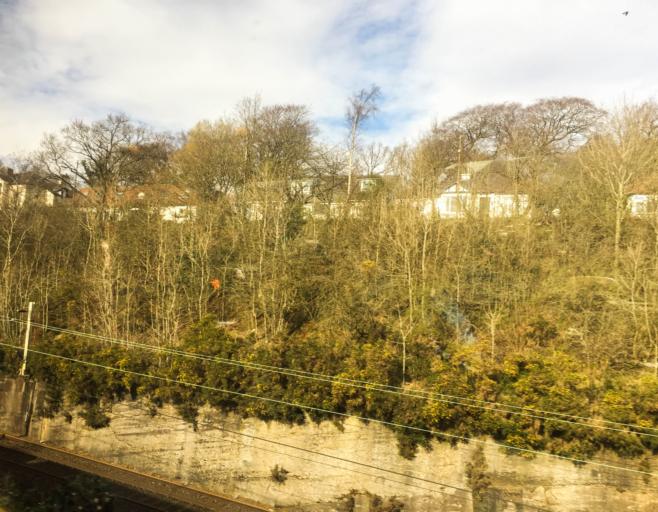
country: GB
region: Scotland
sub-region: East Dunbartonshire
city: Bearsden
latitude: 55.8999
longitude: -4.3246
